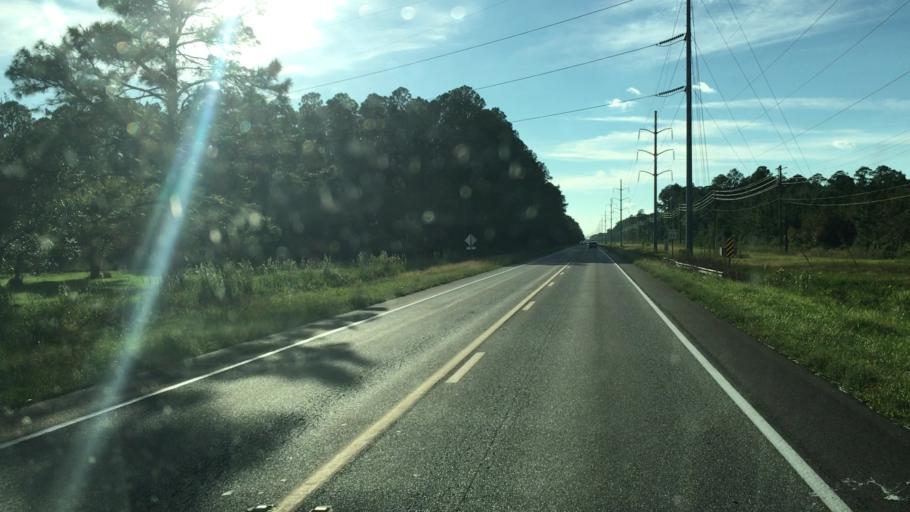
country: US
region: Florida
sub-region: Alachua County
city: Gainesville
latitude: 29.7030
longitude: -82.3070
